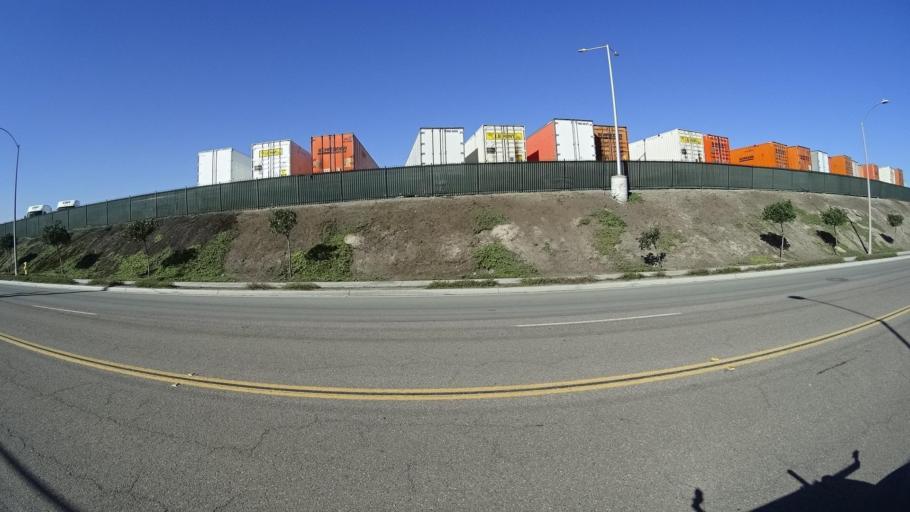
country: MX
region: Baja California
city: Tijuana
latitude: 32.5798
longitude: -116.9190
